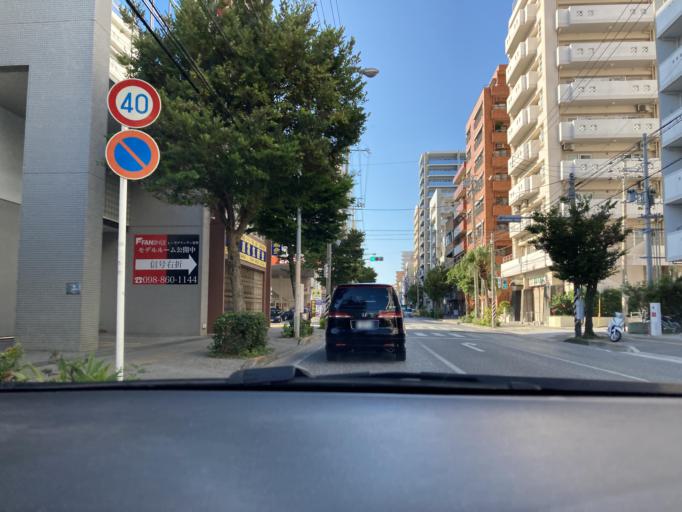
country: JP
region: Okinawa
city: Naha-shi
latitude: 26.2211
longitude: 127.6889
